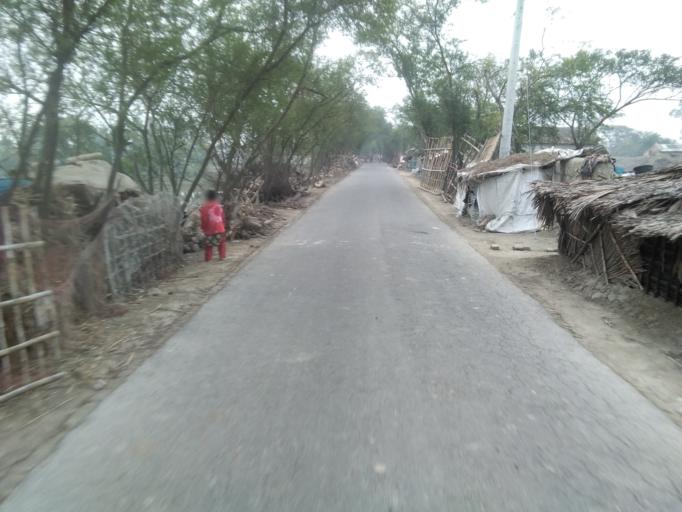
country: BD
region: Khulna
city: Satkhira
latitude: 22.5811
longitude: 89.0683
